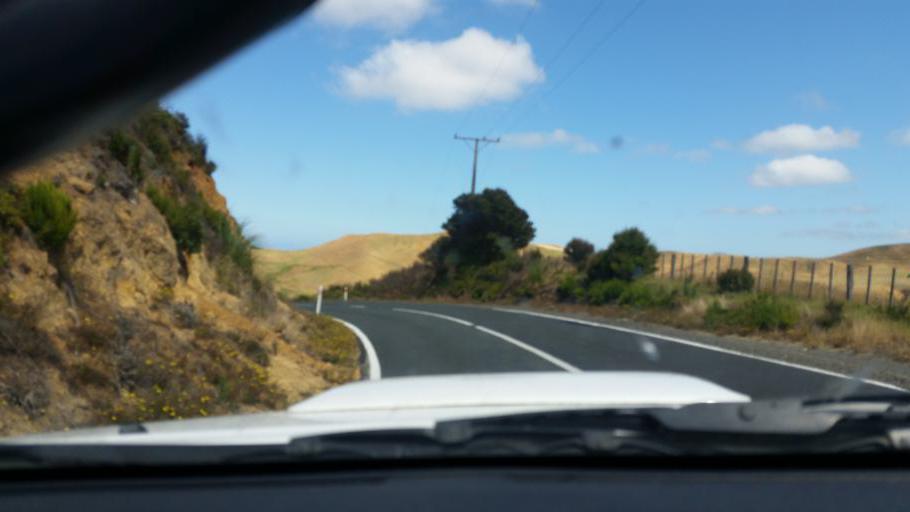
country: NZ
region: Northland
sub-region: Kaipara District
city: Dargaville
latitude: -35.8218
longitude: 173.6874
